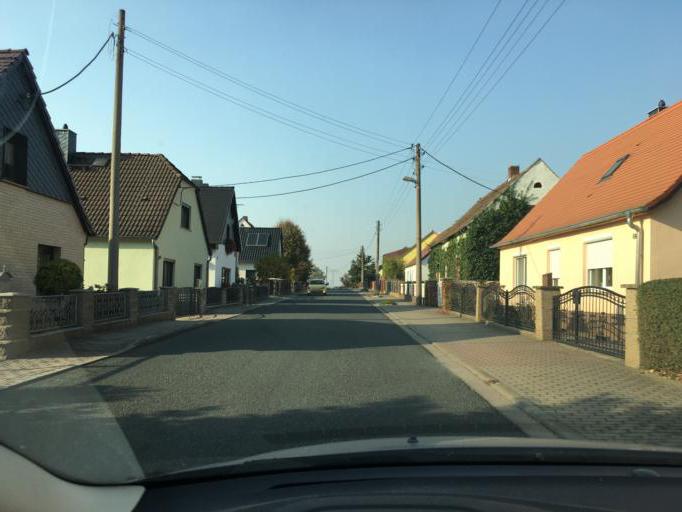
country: DE
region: Saxony
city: Wurzen
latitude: 51.3496
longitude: 12.7599
